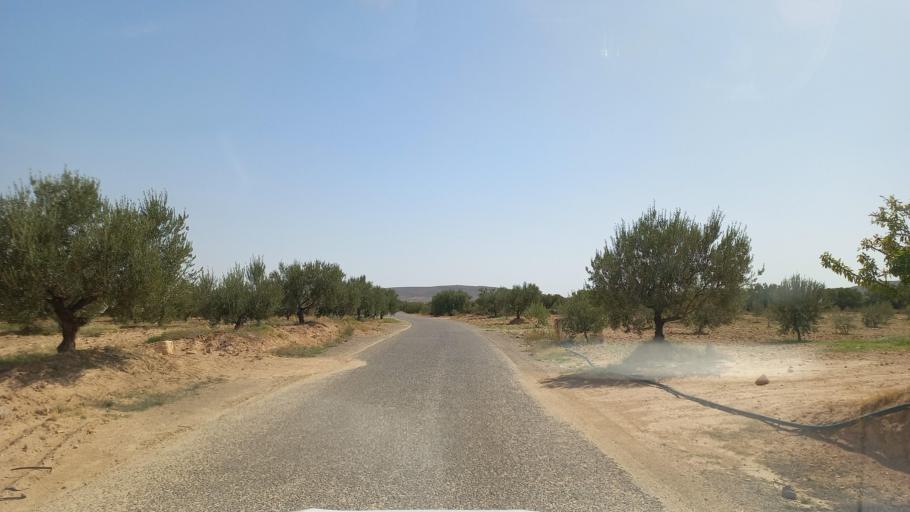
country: TN
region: Al Qasrayn
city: Kasserine
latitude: 35.2176
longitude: 9.0415
